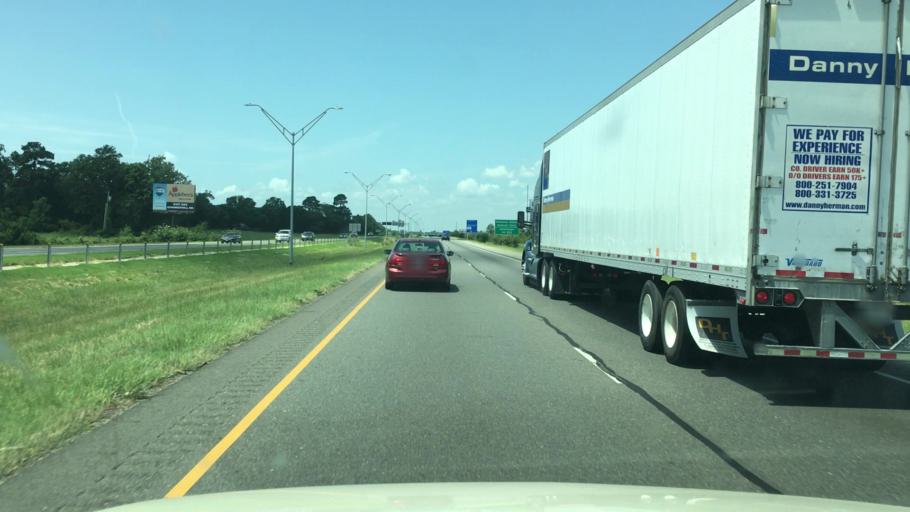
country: US
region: Arkansas
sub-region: Miller County
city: Texarkana
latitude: 33.4747
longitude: -94.0138
